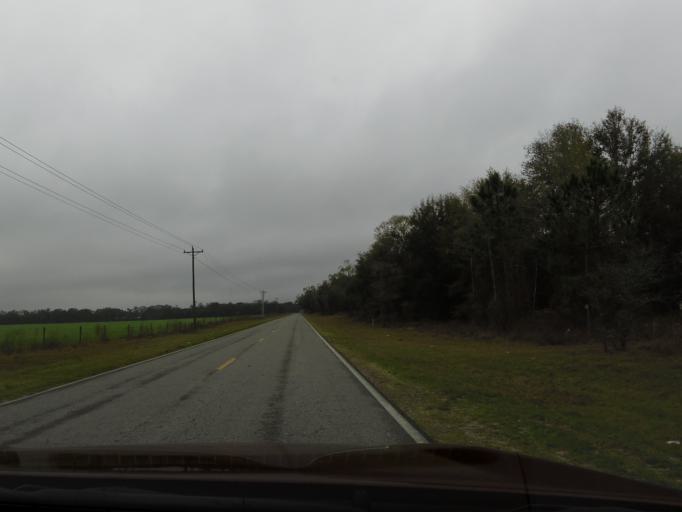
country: US
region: Florida
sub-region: Dixie County
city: Cross City
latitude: 29.8034
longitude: -82.9628
